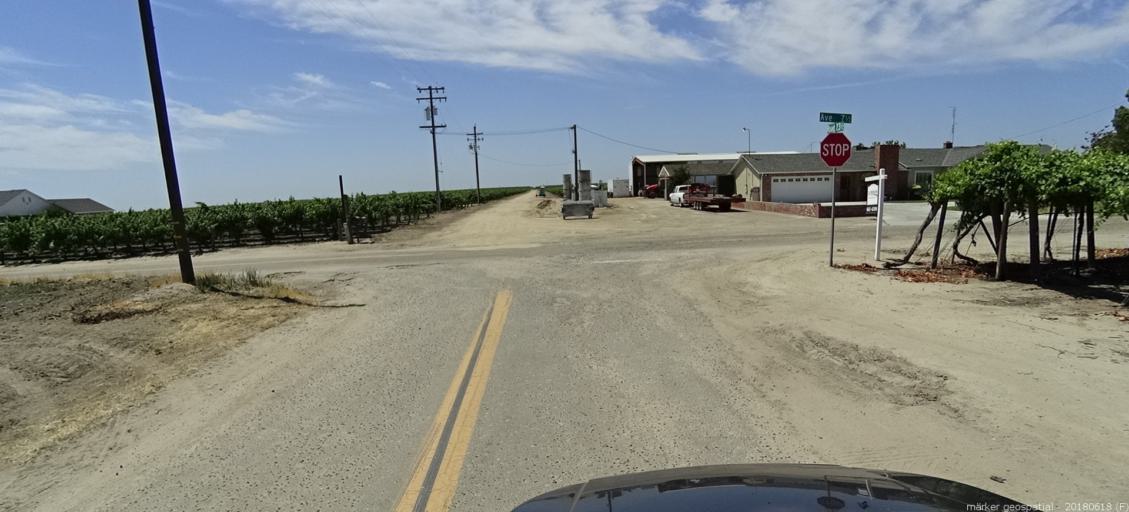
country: US
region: California
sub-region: Madera County
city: Parkwood
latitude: 36.8587
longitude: -120.1194
